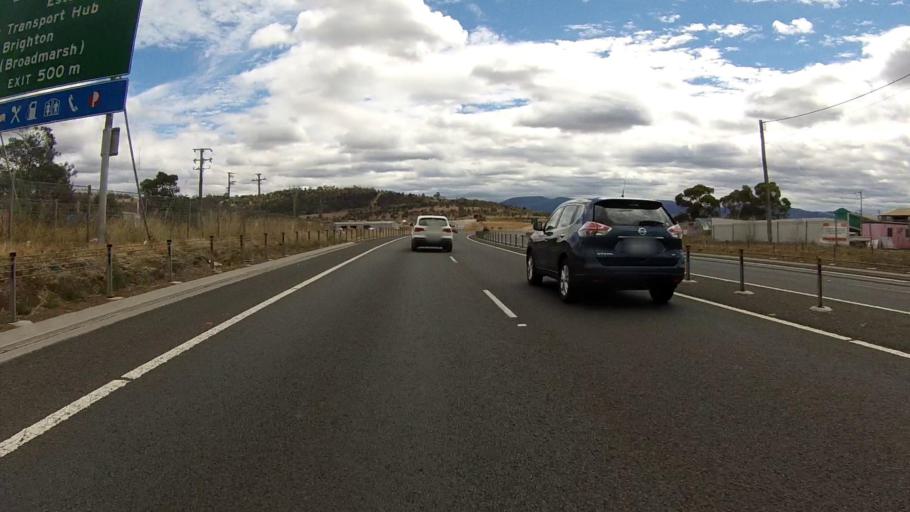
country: AU
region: Tasmania
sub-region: Brighton
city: Bridgewater
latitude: -42.7199
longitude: 147.2378
